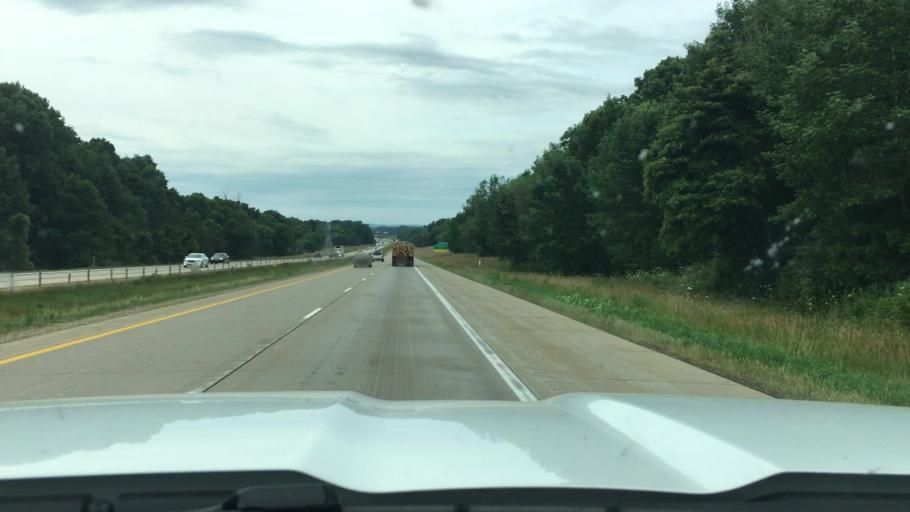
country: US
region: Michigan
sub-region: Allegan County
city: Plainwell
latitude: 42.4855
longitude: -85.6523
